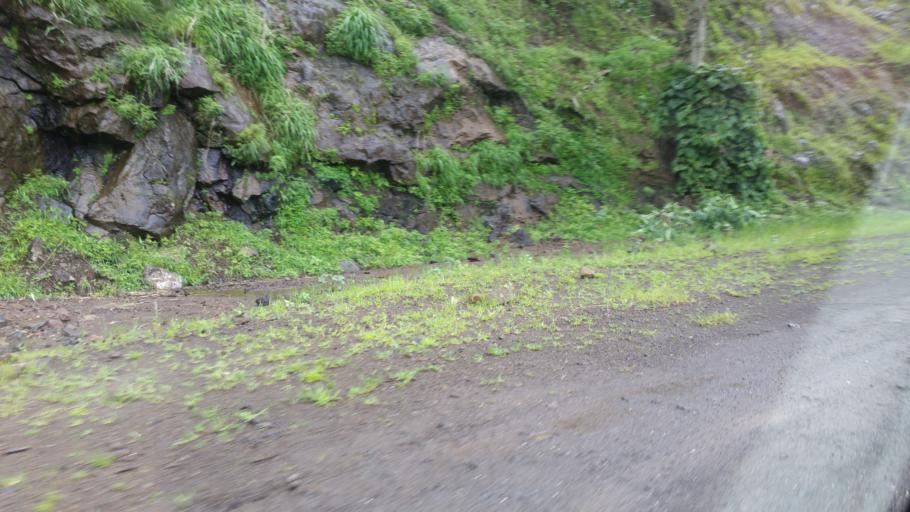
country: ET
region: Amhara
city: Debark'
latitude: 13.3664
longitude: 37.9459
